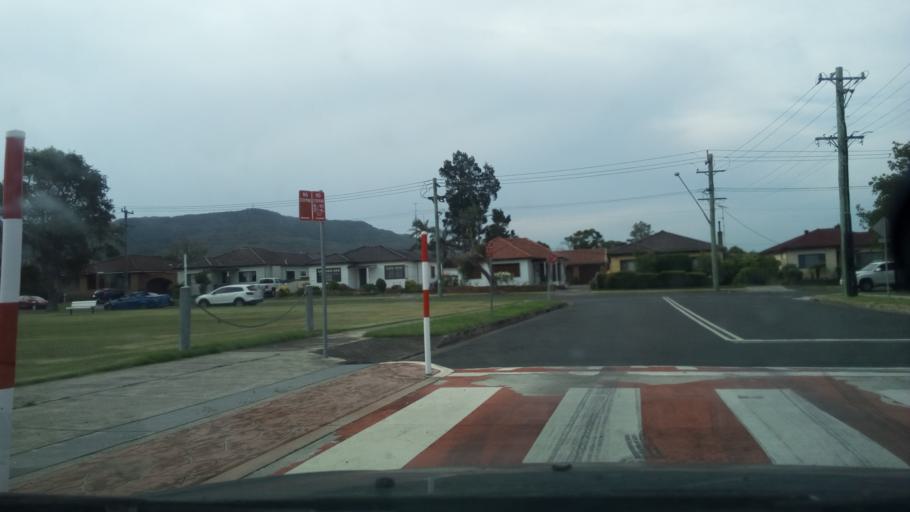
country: AU
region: New South Wales
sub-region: Wollongong
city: Fairy Meadow
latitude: -34.3977
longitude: 150.8898
